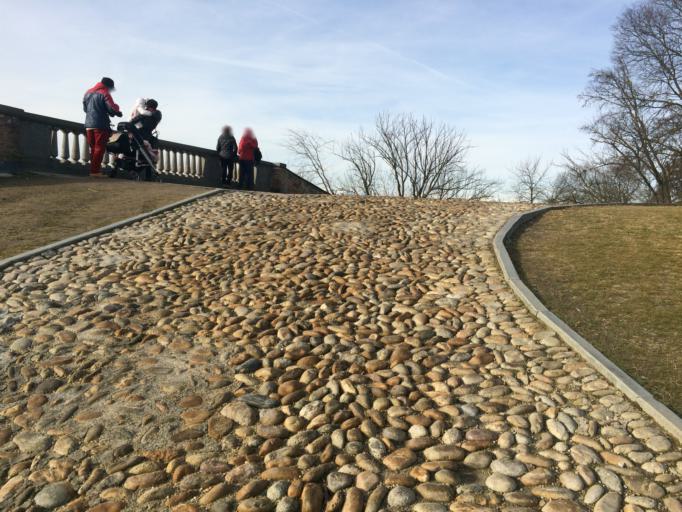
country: IT
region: Piedmont
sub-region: Provincia di Cuneo
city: Govone
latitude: 44.8044
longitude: 8.0999
